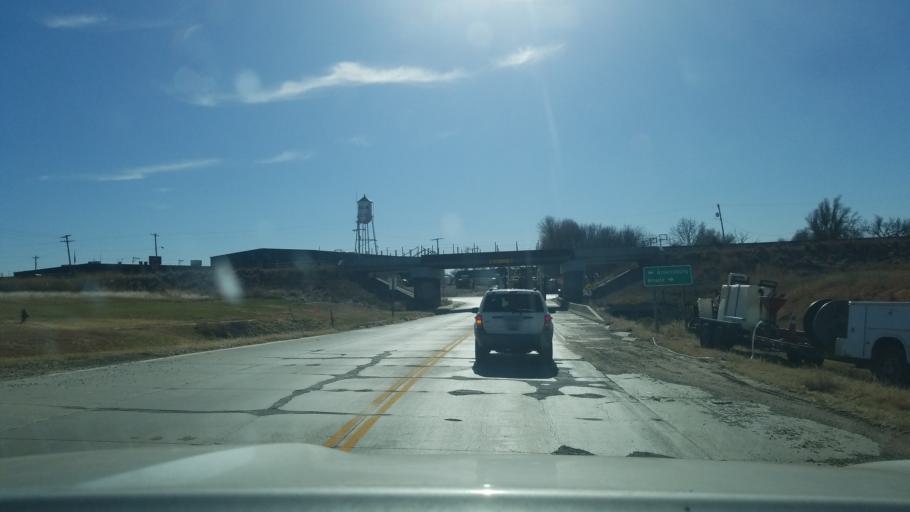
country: US
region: Kansas
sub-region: Kiowa County
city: Greensburg
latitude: 37.5525
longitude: -99.6367
